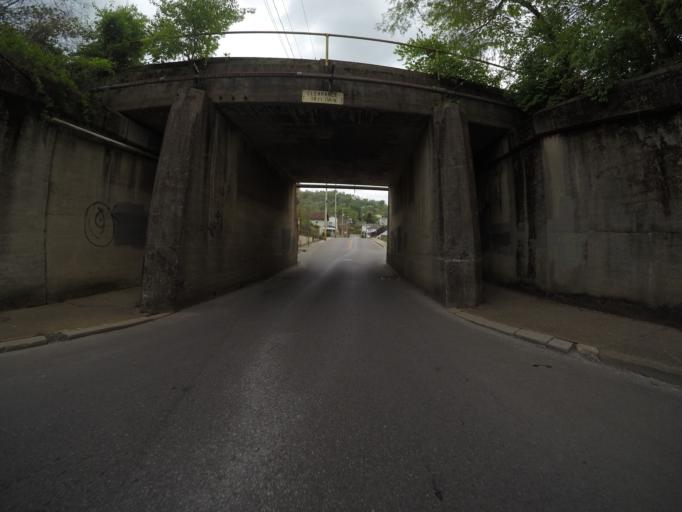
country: US
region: West Virginia
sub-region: Kanawha County
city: Charleston
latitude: 38.3681
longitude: -81.6593
